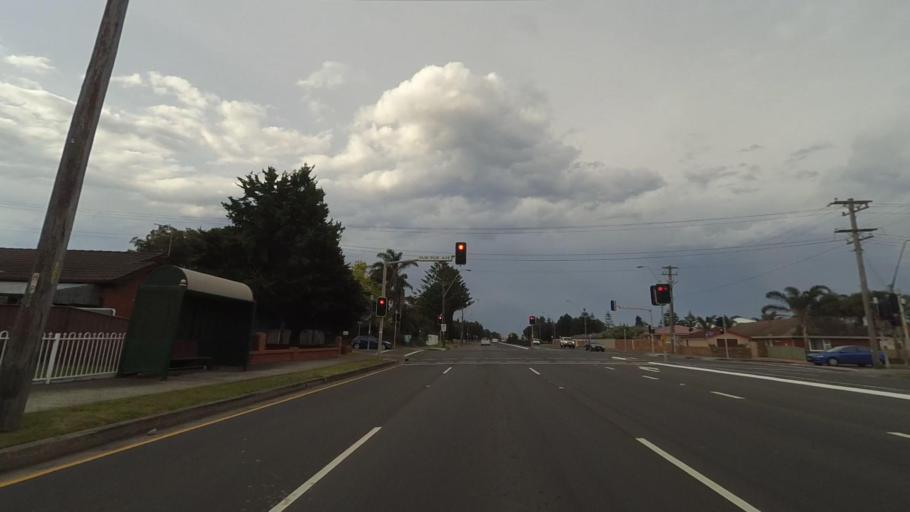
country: AU
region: New South Wales
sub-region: Shellharbour
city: Lake Illawarra
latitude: -34.5412
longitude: 150.8642
